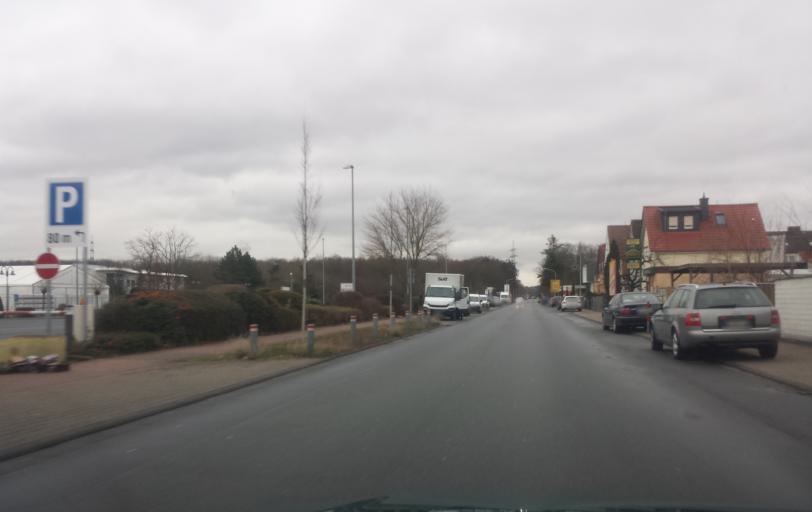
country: DE
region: Hesse
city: Weiterstadt
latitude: 49.8911
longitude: 8.6146
